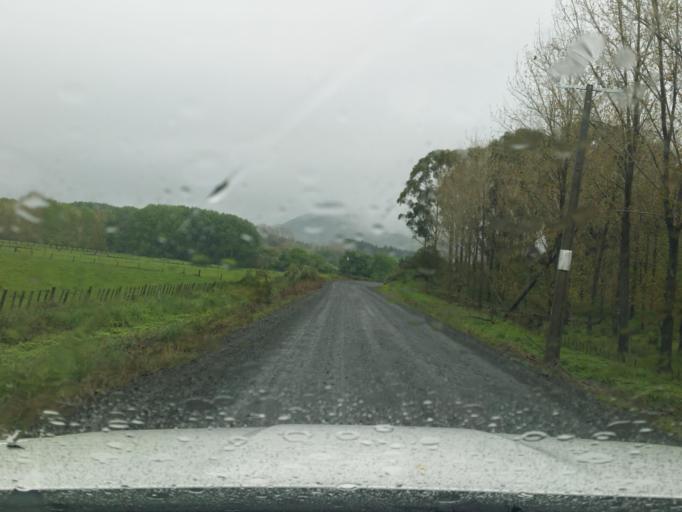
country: NZ
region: Northland
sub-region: Whangarei
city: Maungatapere
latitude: -35.8174
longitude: 174.0385
